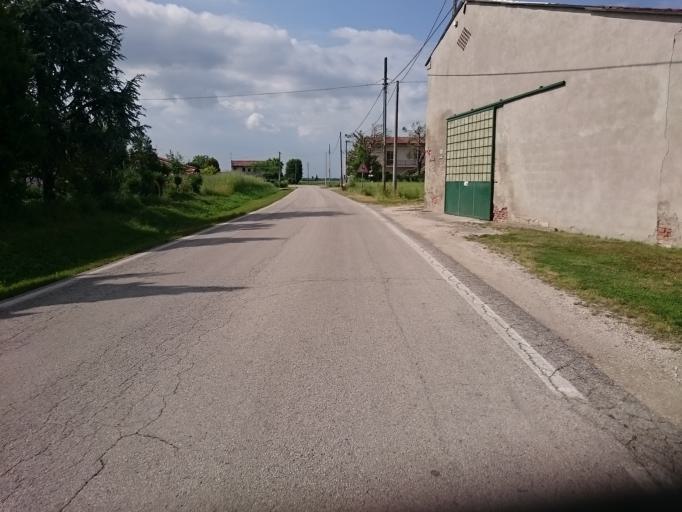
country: IT
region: Veneto
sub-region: Provincia di Padova
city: Casale di Scodosia
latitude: 45.1957
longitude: 11.4910
